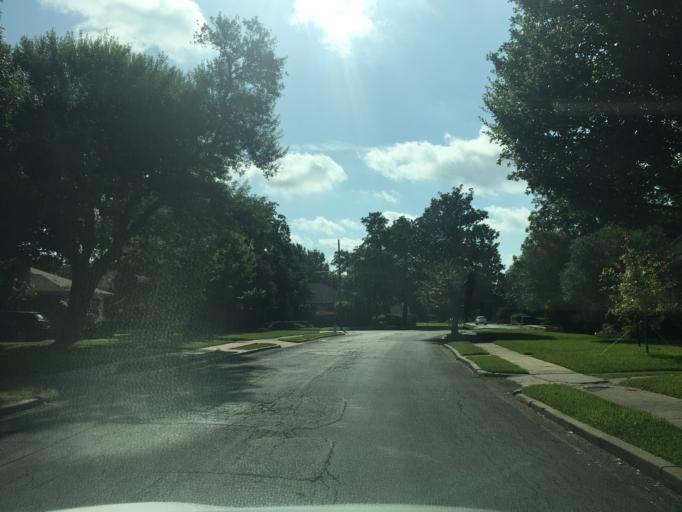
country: US
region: Texas
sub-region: Dallas County
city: Highland Park
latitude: 32.8333
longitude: -96.7590
